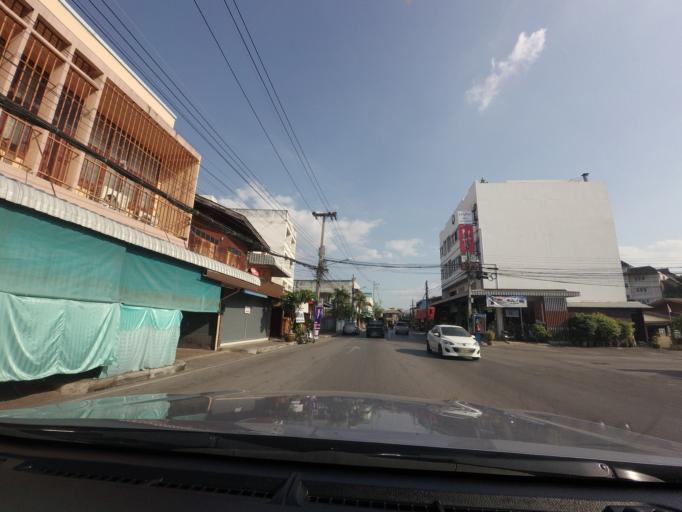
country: TH
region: Lampang
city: Lampang
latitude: 18.2876
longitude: 99.4935
